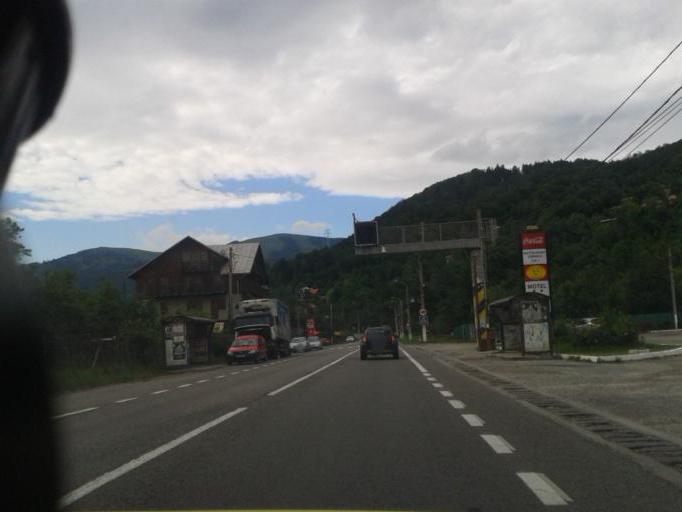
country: RO
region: Prahova
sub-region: Comuna Comarnic
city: Comarnic
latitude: 45.2677
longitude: 25.6240
